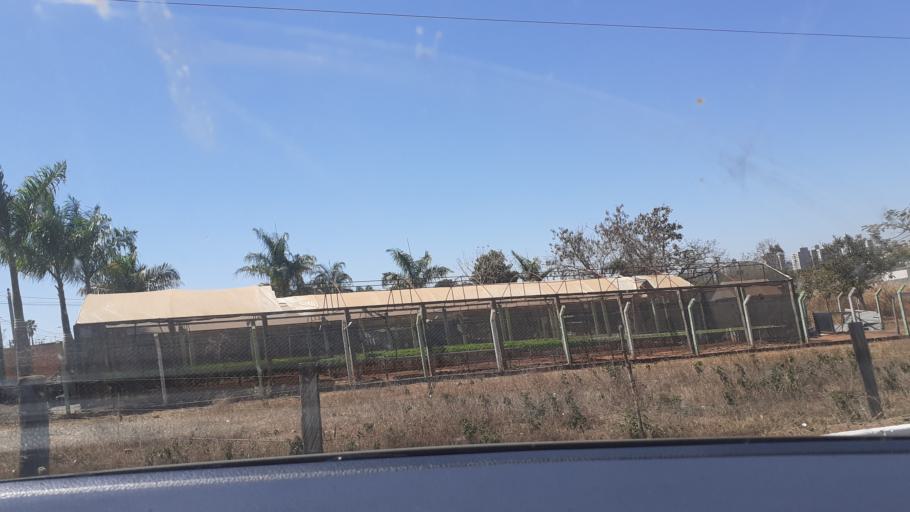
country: BR
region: Goias
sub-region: Caldas Novas
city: Caldas Novas
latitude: -17.7425
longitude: -48.6455
